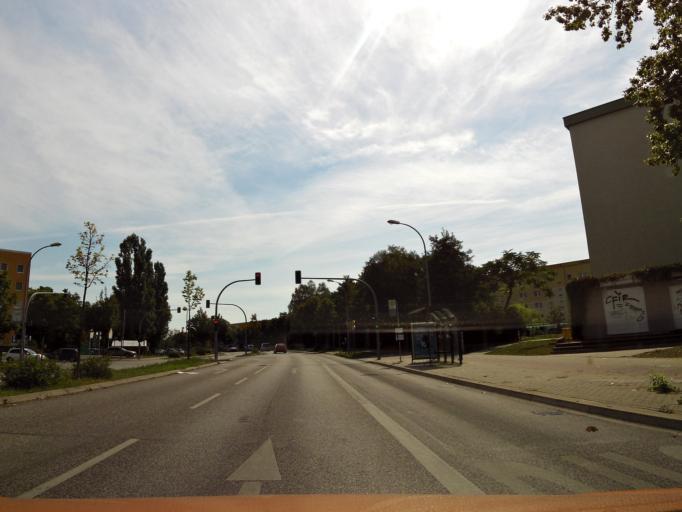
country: DE
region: Brandenburg
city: Teltow
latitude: 52.3994
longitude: 13.2711
